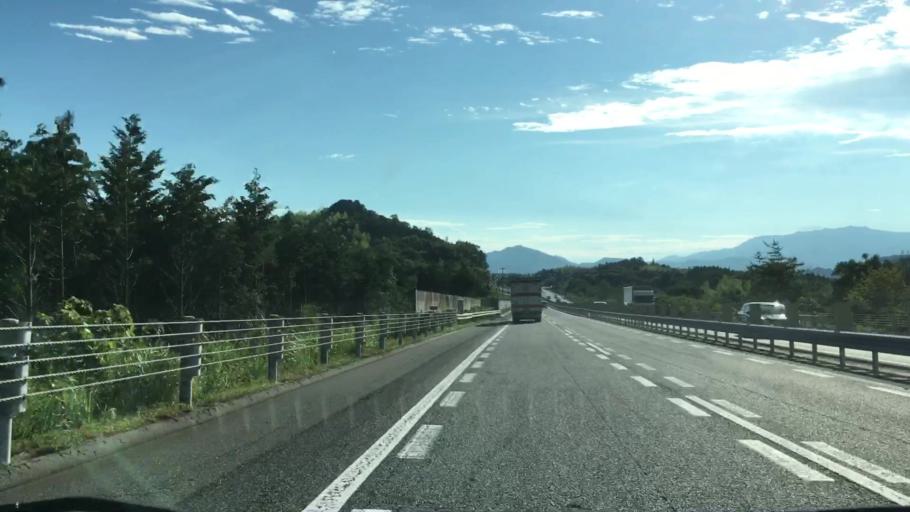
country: JP
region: Yamaguchi
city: Iwakuni
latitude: 34.1031
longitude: 132.1092
